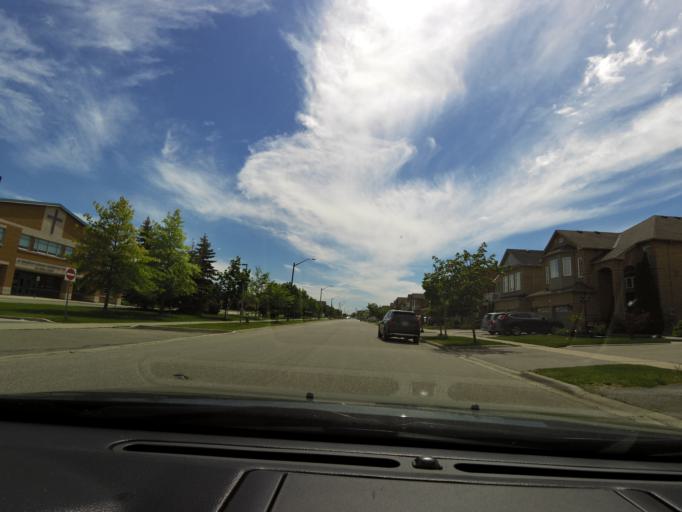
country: CA
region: Ontario
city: Mississauga
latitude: 43.5416
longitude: -79.7230
